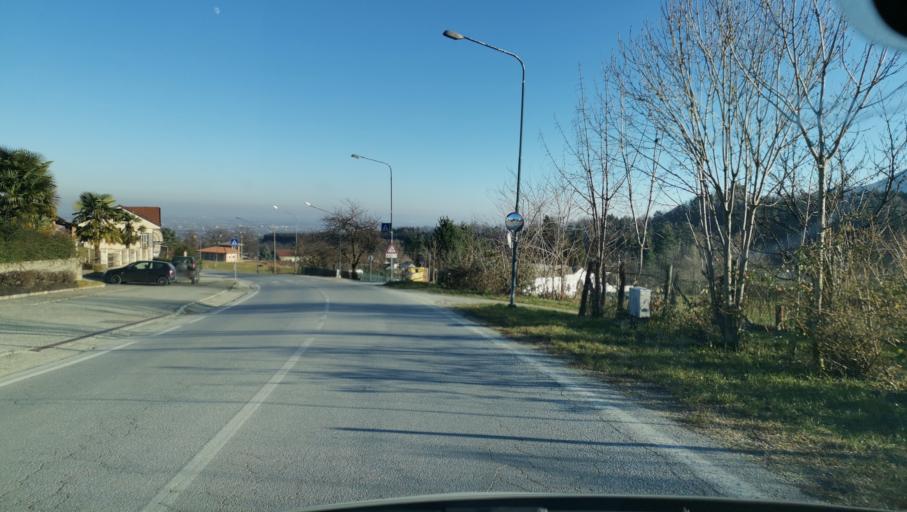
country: IT
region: Piedmont
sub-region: Provincia di Cuneo
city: Bagnolo Piemonte
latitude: 44.7528
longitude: 7.2916
